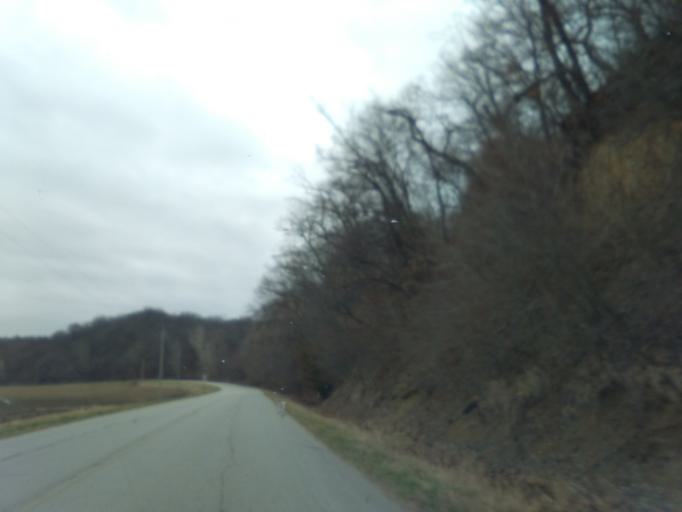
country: US
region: Missouri
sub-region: Holt County
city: Mound City
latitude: 40.0079
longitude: -95.3358
